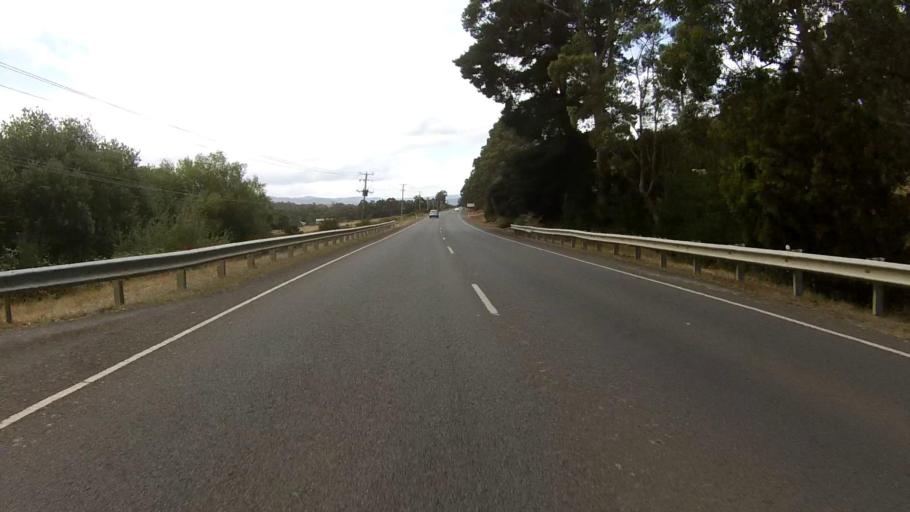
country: AU
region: Tasmania
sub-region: Kingborough
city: Kettering
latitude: -43.0861
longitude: 147.2518
